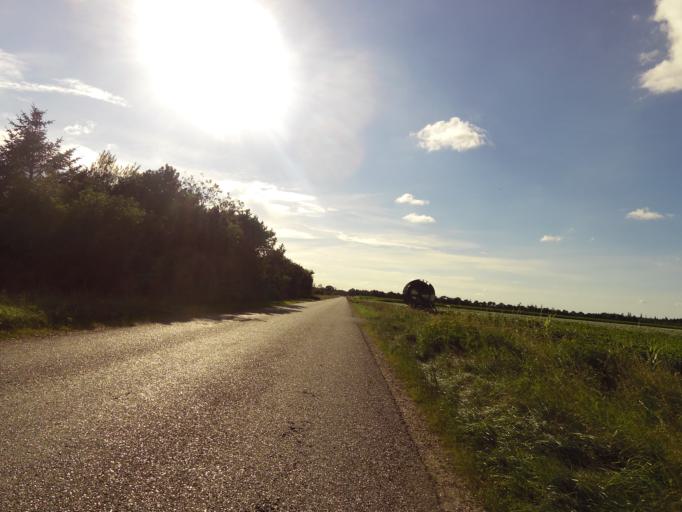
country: DK
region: South Denmark
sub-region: Haderslev Kommune
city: Vojens
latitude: 55.2072
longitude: 9.2649
